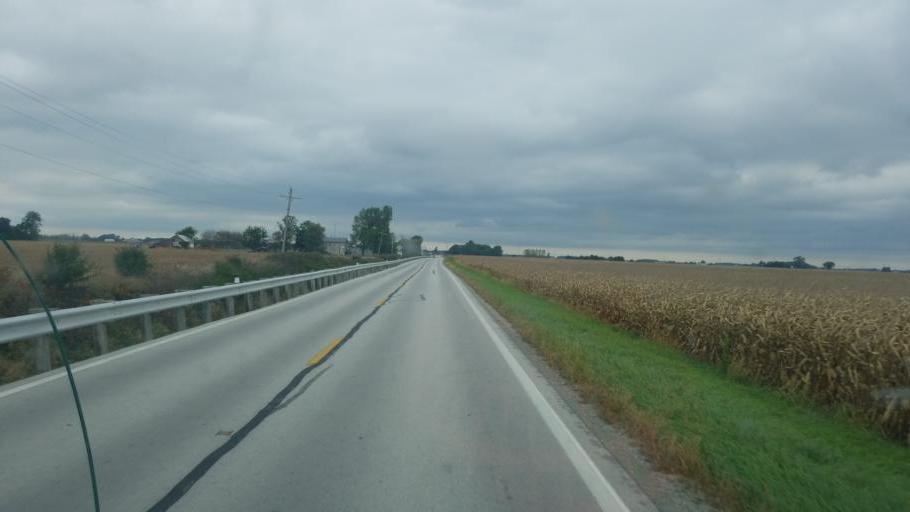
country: US
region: Ohio
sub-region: Wood County
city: Haskins
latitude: 41.4395
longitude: -83.6974
